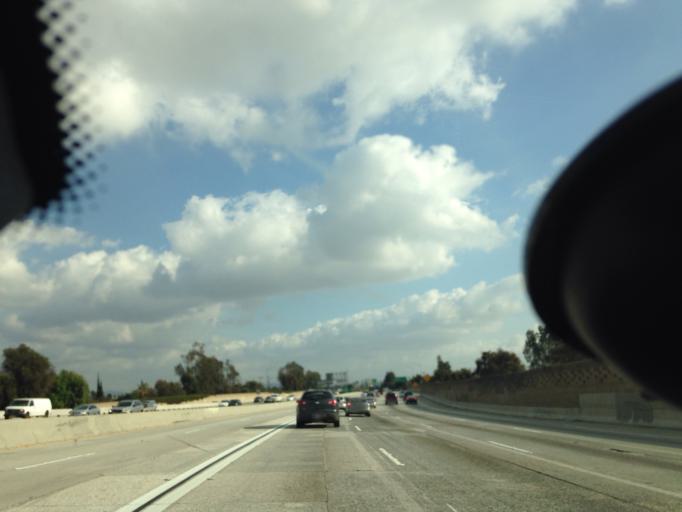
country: US
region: California
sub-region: Los Angeles County
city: El Monte
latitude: 34.0677
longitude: -118.0211
